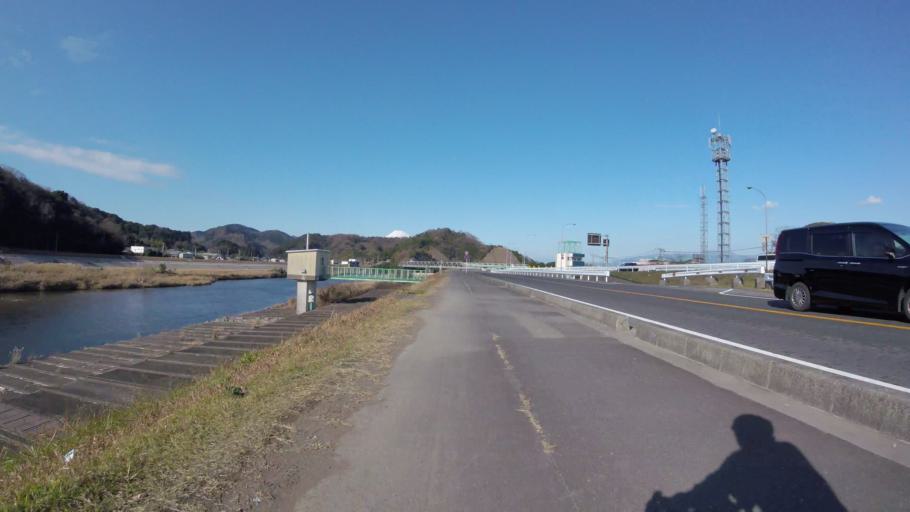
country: JP
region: Shizuoka
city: Mishima
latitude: 35.0163
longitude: 138.9397
